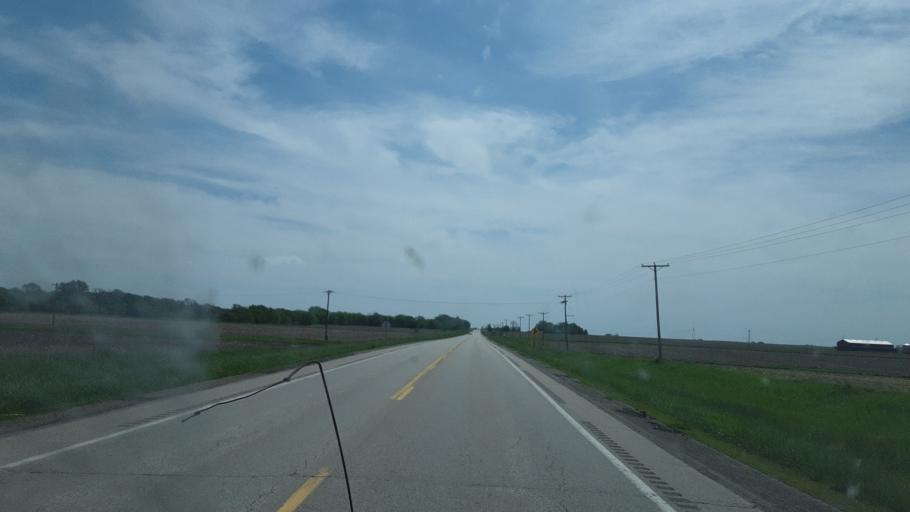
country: US
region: Illinois
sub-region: McLean County
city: Heyworth
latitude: 40.3121
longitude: -88.9633
